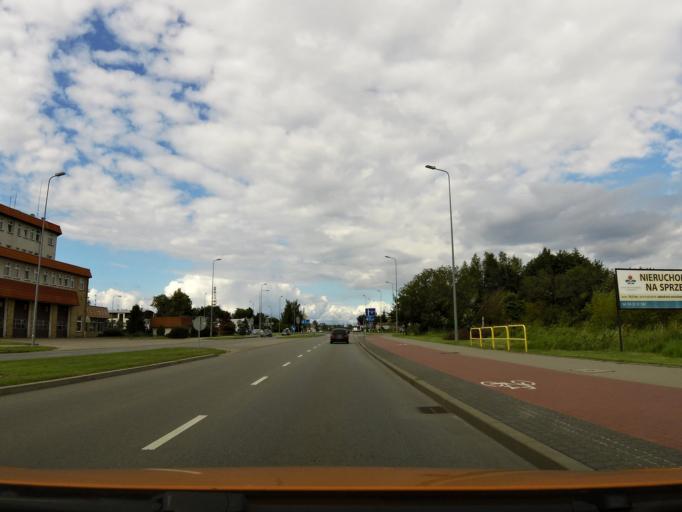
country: PL
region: West Pomeranian Voivodeship
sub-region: Powiat kolobrzeski
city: Kolobrzeg
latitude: 54.1674
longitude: 15.5529
